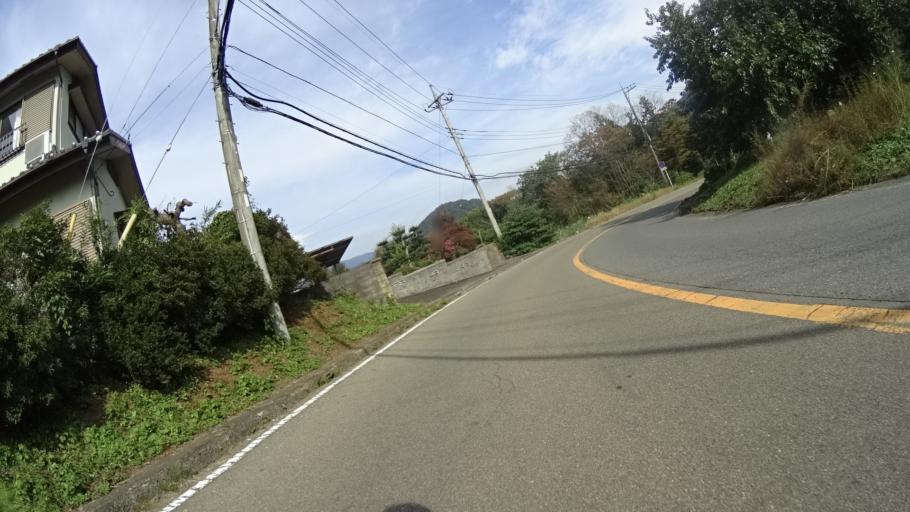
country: JP
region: Yamanashi
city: Uenohara
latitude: 35.5892
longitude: 139.1477
